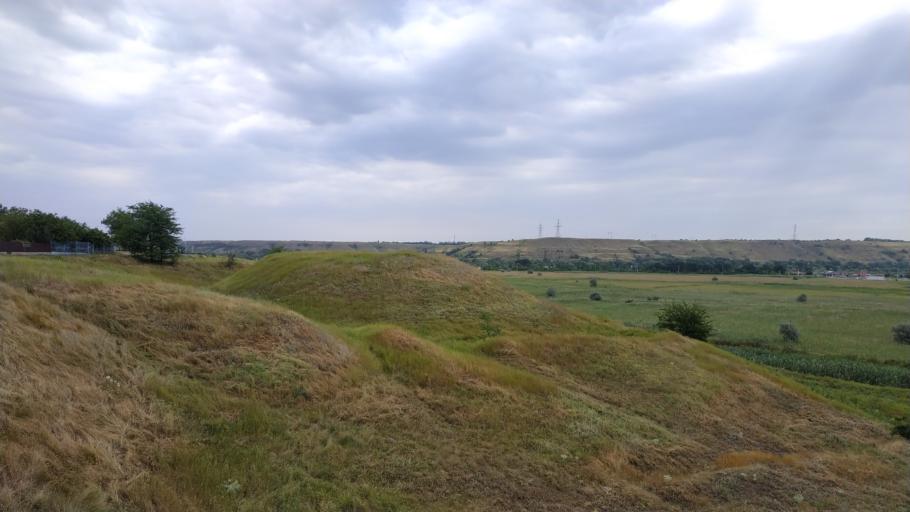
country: RU
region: Krasnodarskiy
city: Krasnaya Polyana
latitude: 45.0253
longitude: 41.1041
